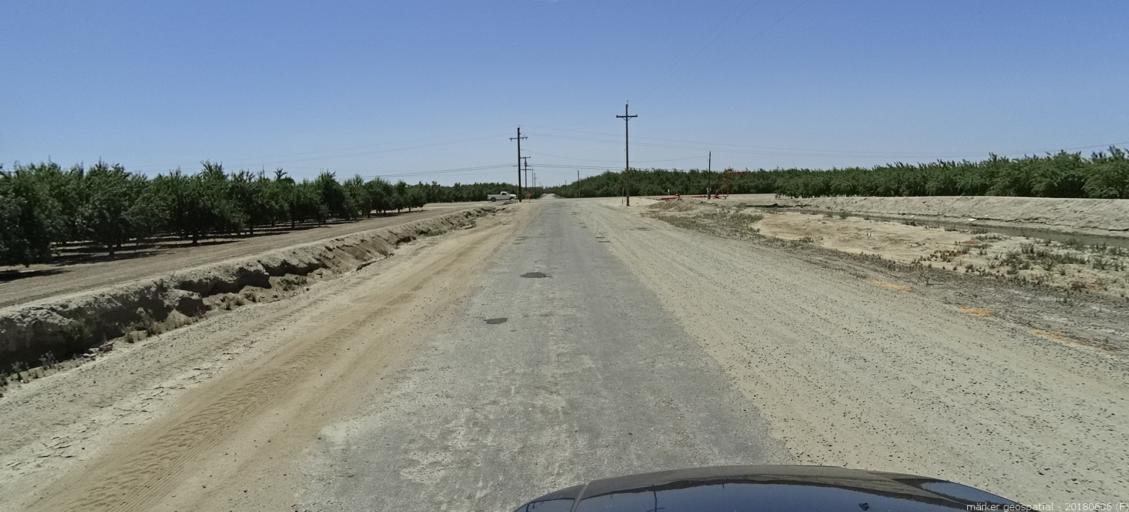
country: US
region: California
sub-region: Fresno County
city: Firebaugh
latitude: 36.8595
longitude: -120.3998
